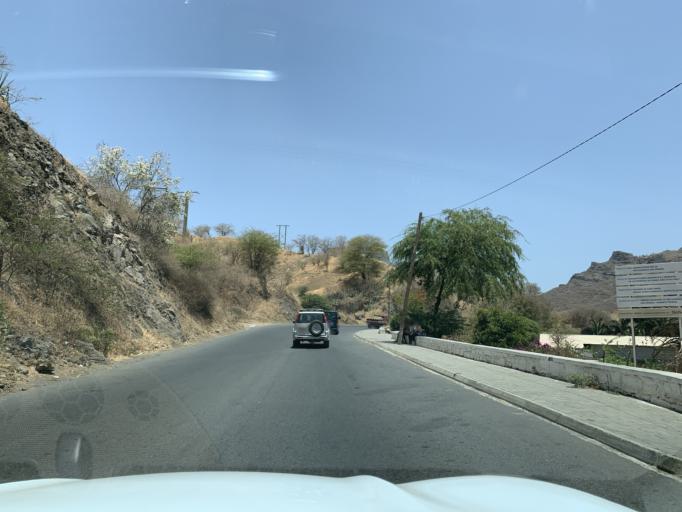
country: CV
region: Sao Lourenco dos Orgaos
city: Joao Teves
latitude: 15.0678
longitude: -23.5821
